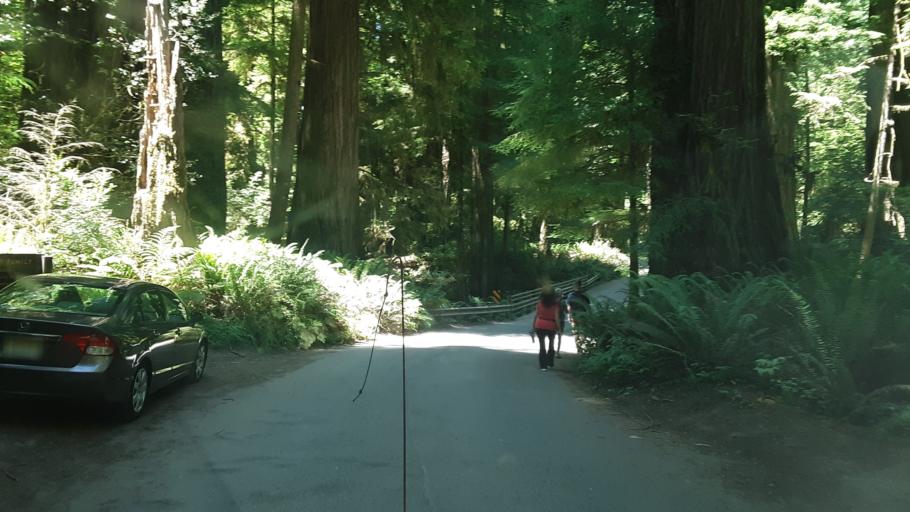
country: US
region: California
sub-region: Del Norte County
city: Bertsch-Oceanview
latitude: 41.8124
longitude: -124.1089
